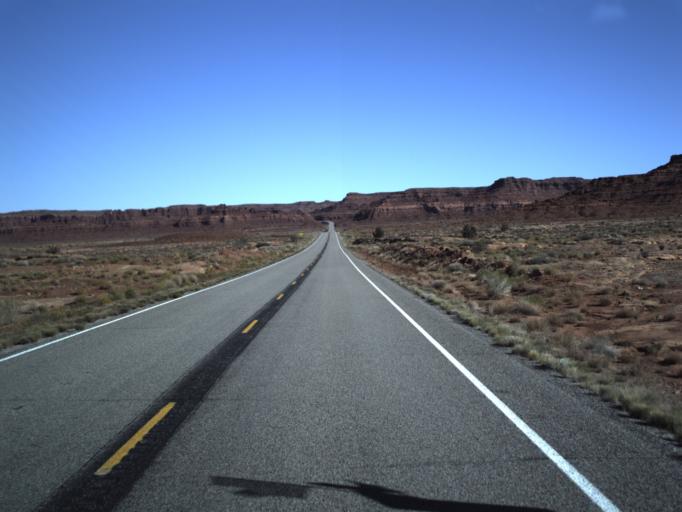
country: US
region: Utah
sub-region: San Juan County
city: Blanding
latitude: 37.8302
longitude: -110.3581
